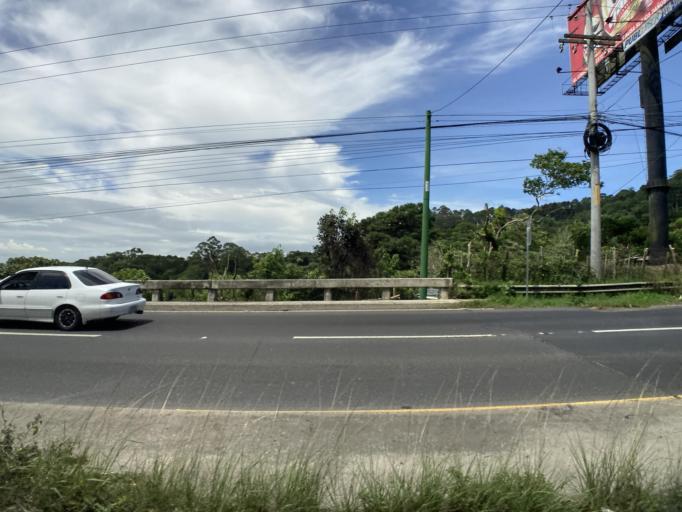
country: GT
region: Guatemala
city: Santa Catarina Pinula
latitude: 14.5799
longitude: -90.4723
